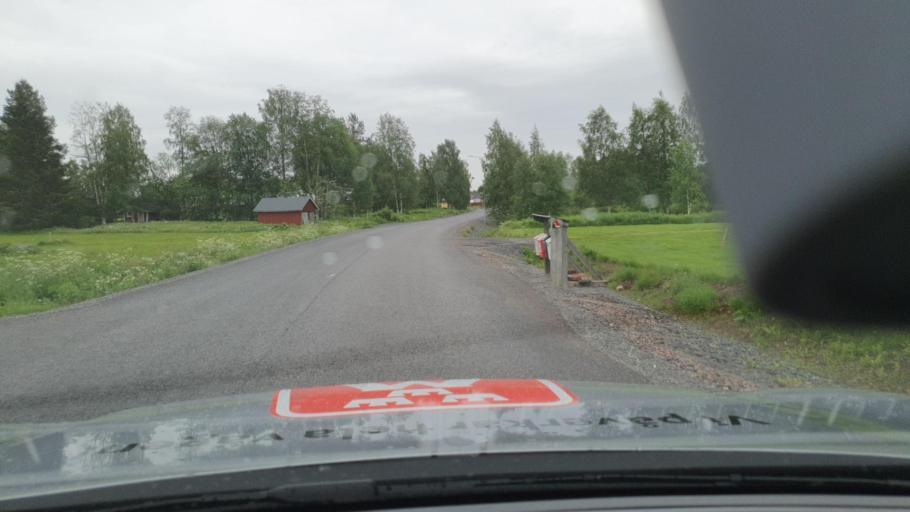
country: SE
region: Norrbotten
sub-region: Pajala Kommun
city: Pajala
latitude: 66.7327
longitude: 23.1751
